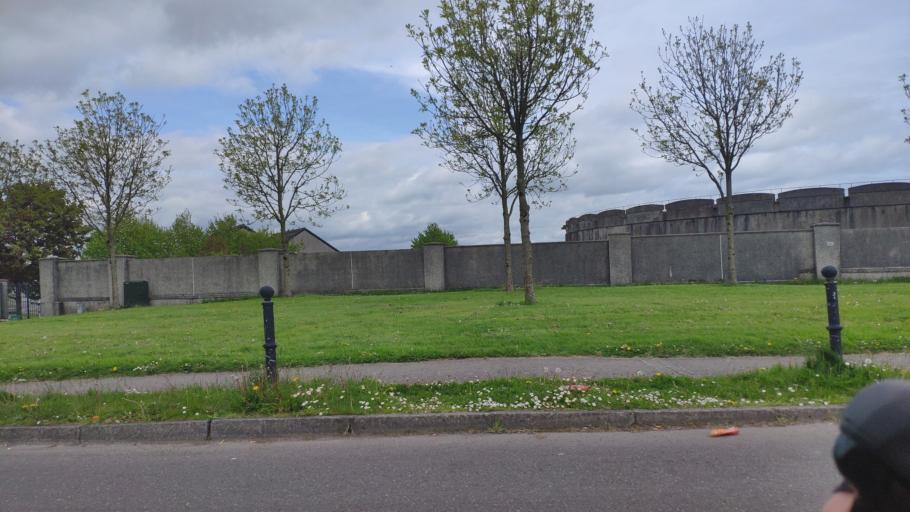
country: IE
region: Munster
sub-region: County Cork
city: Cork
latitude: 51.9092
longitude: -8.5056
